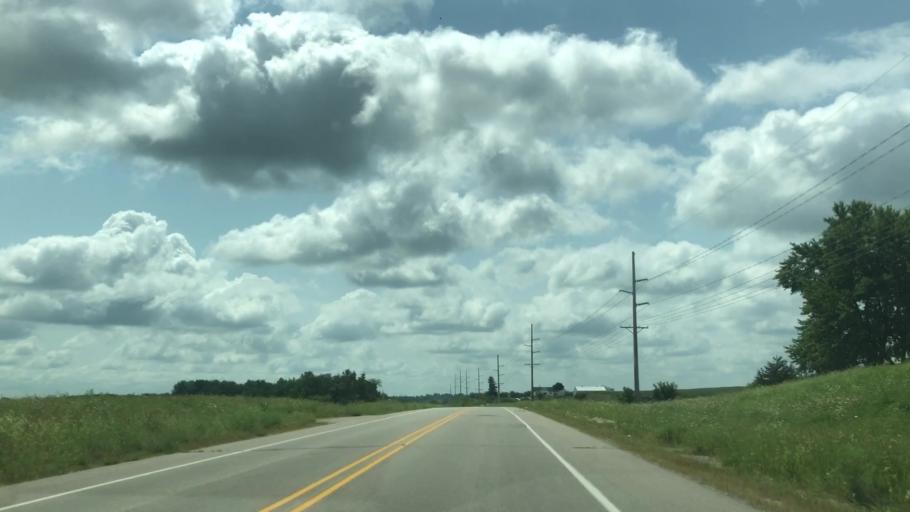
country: US
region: Iowa
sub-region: Marshall County
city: Marshalltown
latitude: 42.0312
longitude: -92.9603
